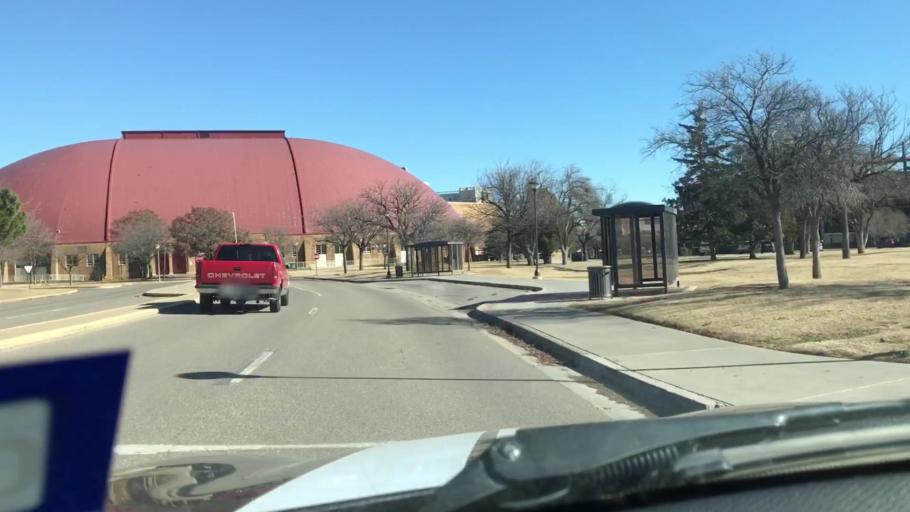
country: US
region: Texas
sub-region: Lubbock County
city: Lubbock
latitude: 33.5891
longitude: -101.8793
